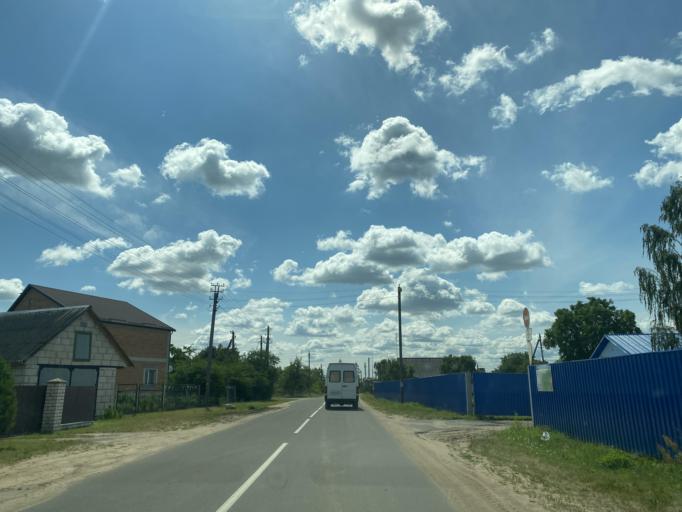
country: BY
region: Brest
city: Ivanava
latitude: 52.1438
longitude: 25.5467
